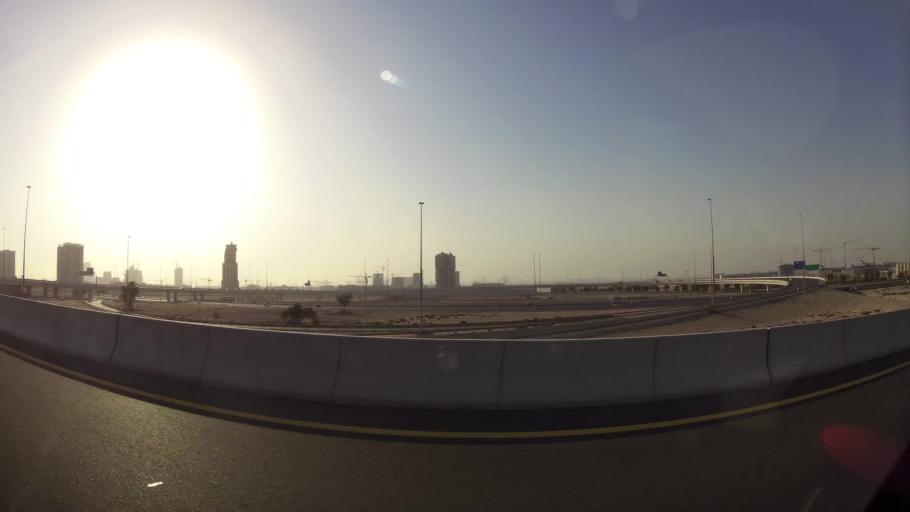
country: AE
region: Dubai
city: Dubai
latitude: 25.0500
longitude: 55.2260
